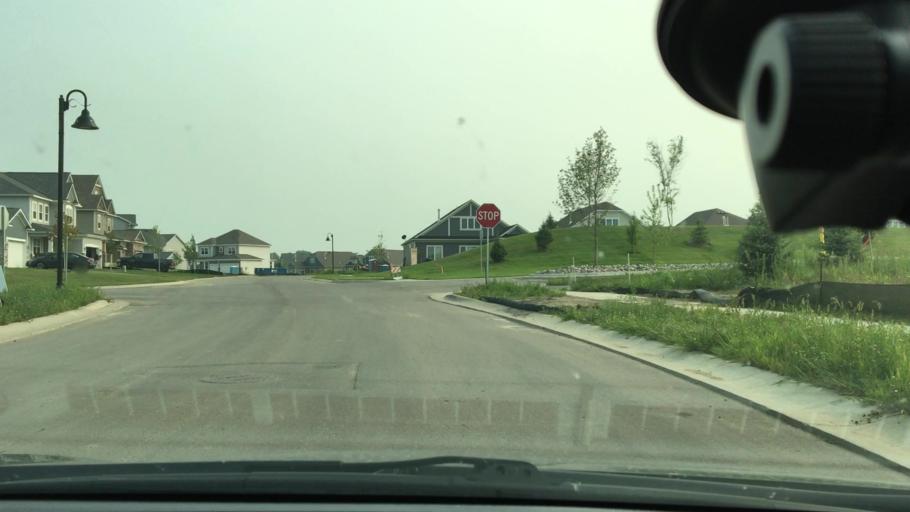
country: US
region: Minnesota
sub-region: Anoka County
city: Ramsey
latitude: 45.2168
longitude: -93.4659
